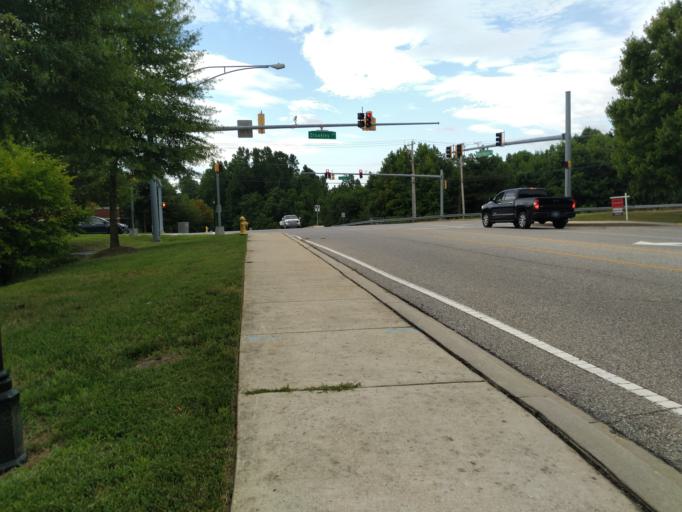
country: US
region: Maryland
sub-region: Calvert County
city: Prince Frederick
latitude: 38.5578
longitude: -76.6031
